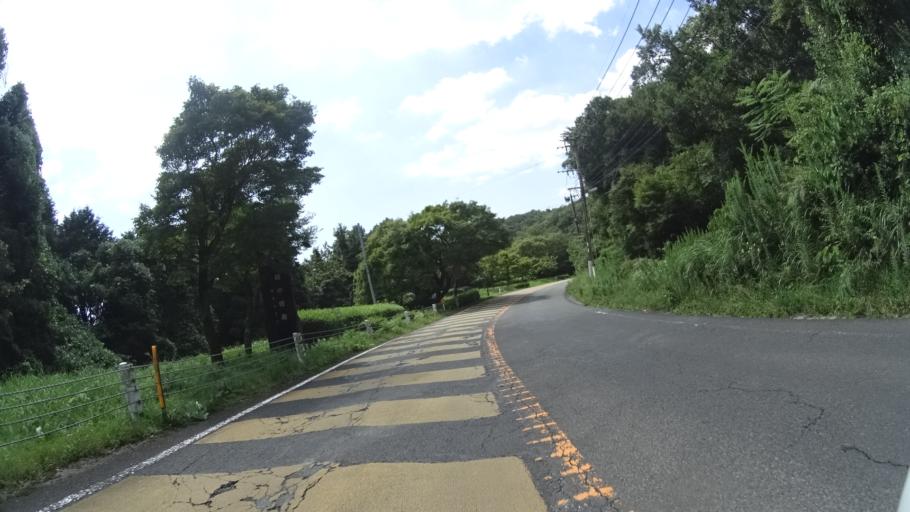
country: JP
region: Kagoshima
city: Kokubu-matsuki
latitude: 31.8730
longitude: 130.7940
